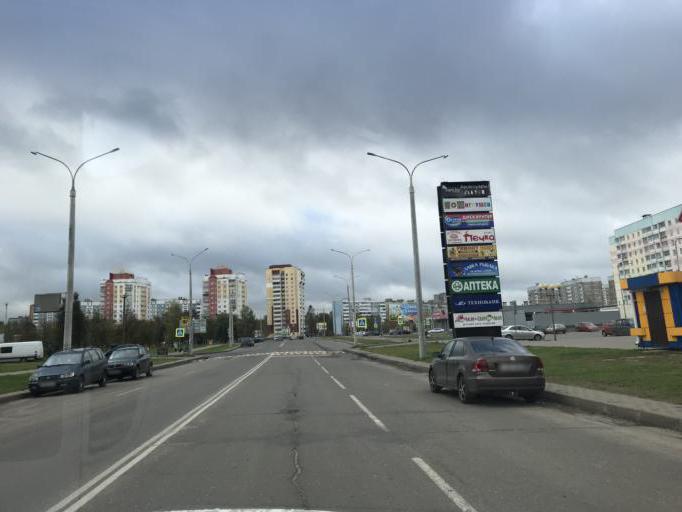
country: BY
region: Mogilev
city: Mahilyow
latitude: 53.8820
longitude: 30.3684
